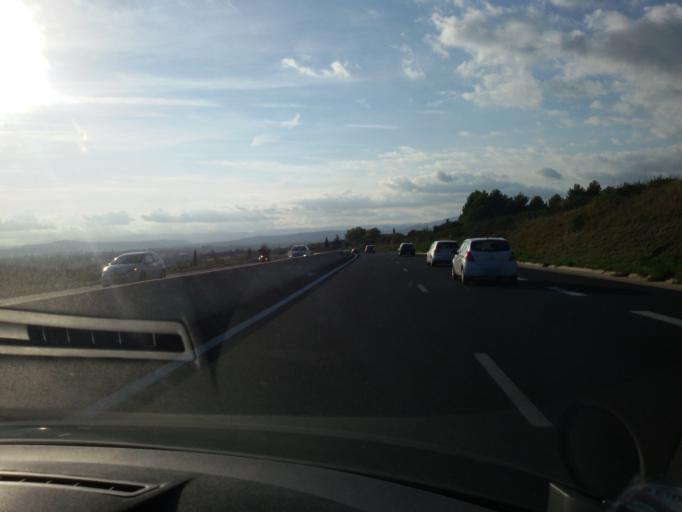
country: FR
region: Languedoc-Roussillon
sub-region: Departement de l'Herault
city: Gignac
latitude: 43.6431
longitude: 3.5661
